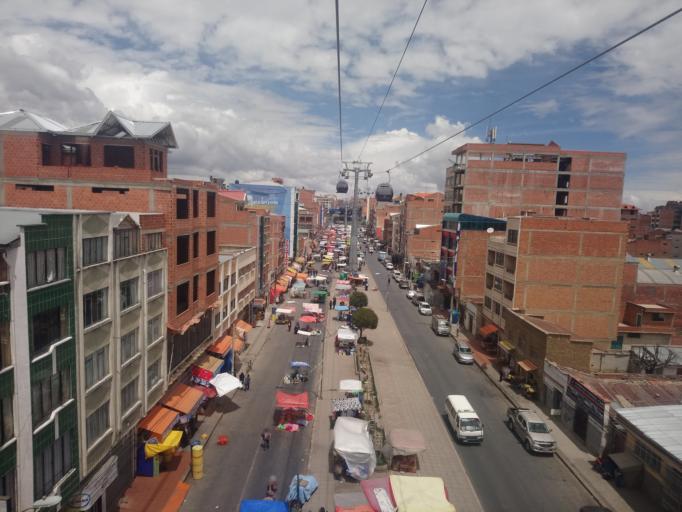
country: BO
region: La Paz
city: La Paz
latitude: -16.4939
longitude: -68.1769
